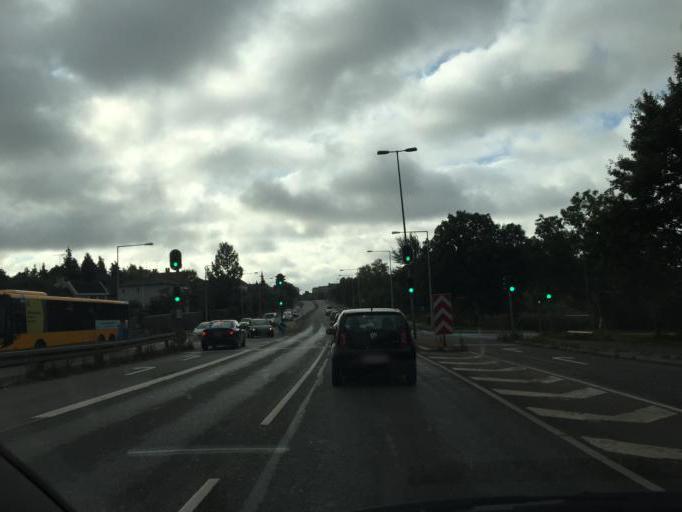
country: DK
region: Capital Region
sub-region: Kobenhavn
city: Vanlose
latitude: 55.7131
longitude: 12.5042
